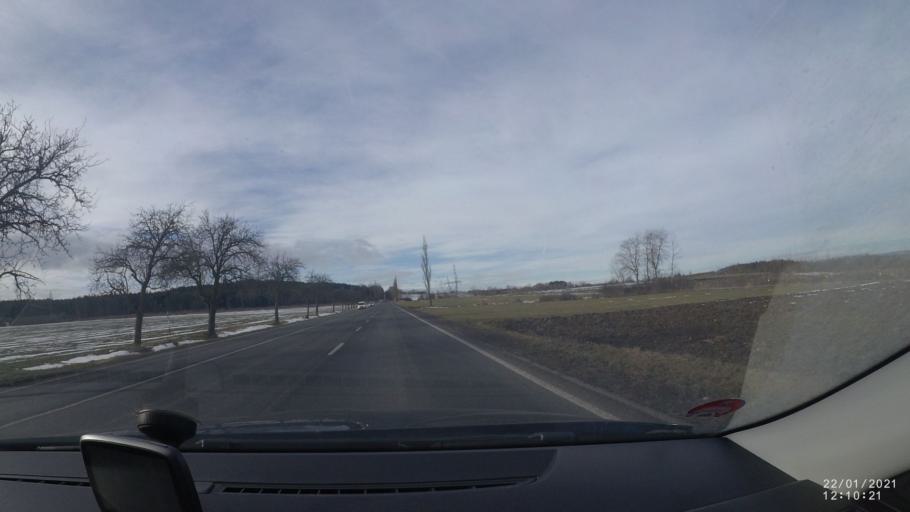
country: CZ
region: Plzensky
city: Dysina
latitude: 49.7453
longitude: 13.5057
